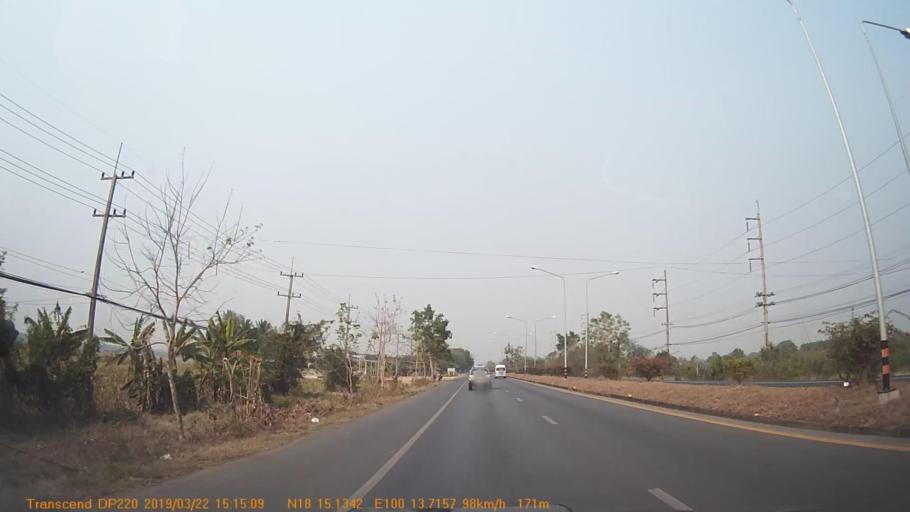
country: TH
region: Phrae
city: Nong Muang Khai
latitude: 18.2526
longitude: 100.2289
